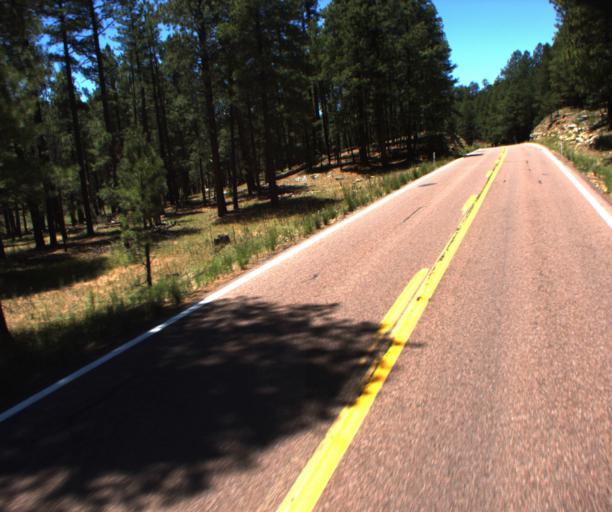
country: US
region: Arizona
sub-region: Gila County
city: Pine
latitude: 34.5366
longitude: -111.3356
